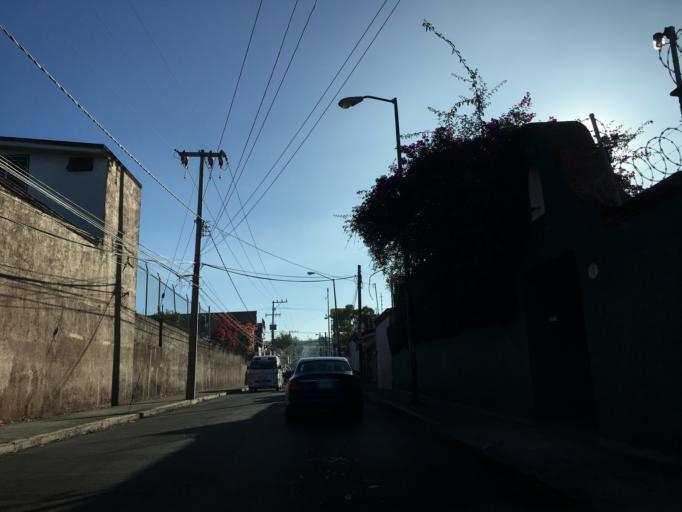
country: MX
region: Michoacan
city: Morelia
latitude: 19.6778
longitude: -101.2013
